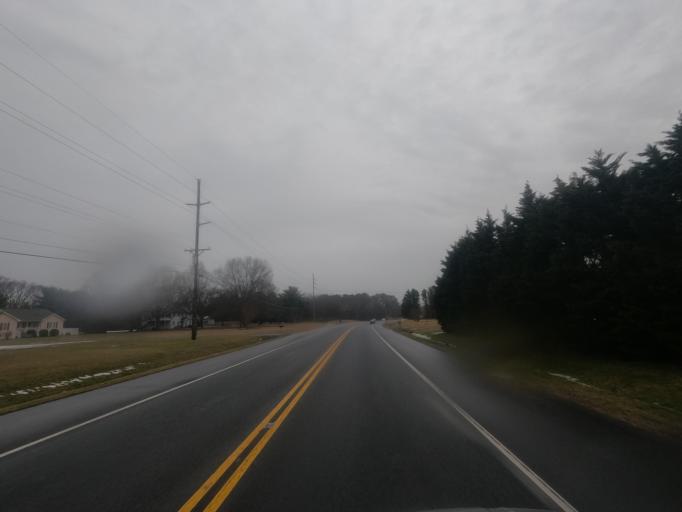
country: US
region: Maryland
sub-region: Dorchester County
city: Cambridge
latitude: 38.5674
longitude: -75.9892
